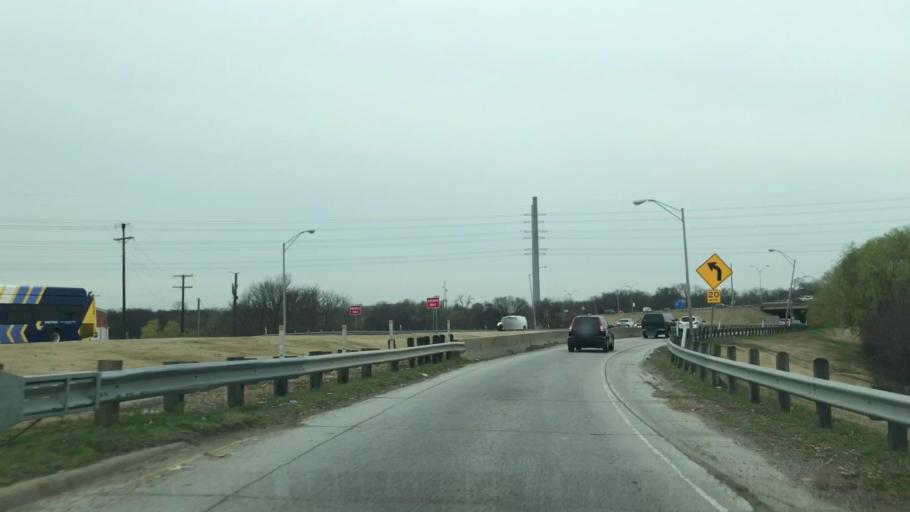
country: US
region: Texas
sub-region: Dallas County
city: University Park
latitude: 32.8475
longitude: -96.8769
